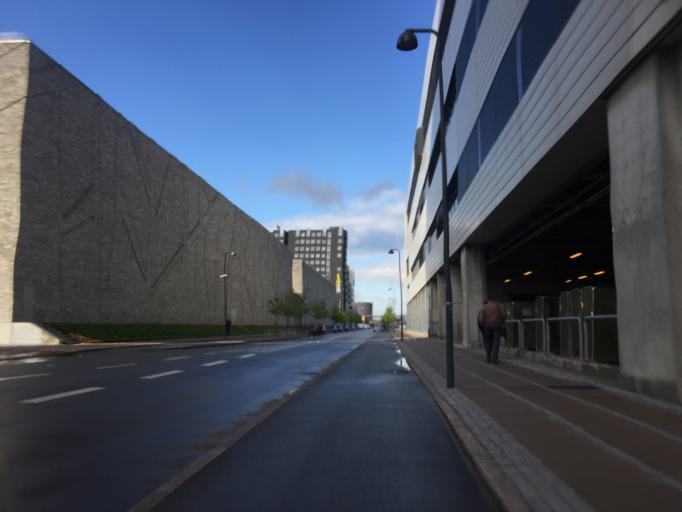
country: DK
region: Capital Region
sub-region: Kobenhavn
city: Copenhagen
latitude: 55.6688
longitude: 12.5698
